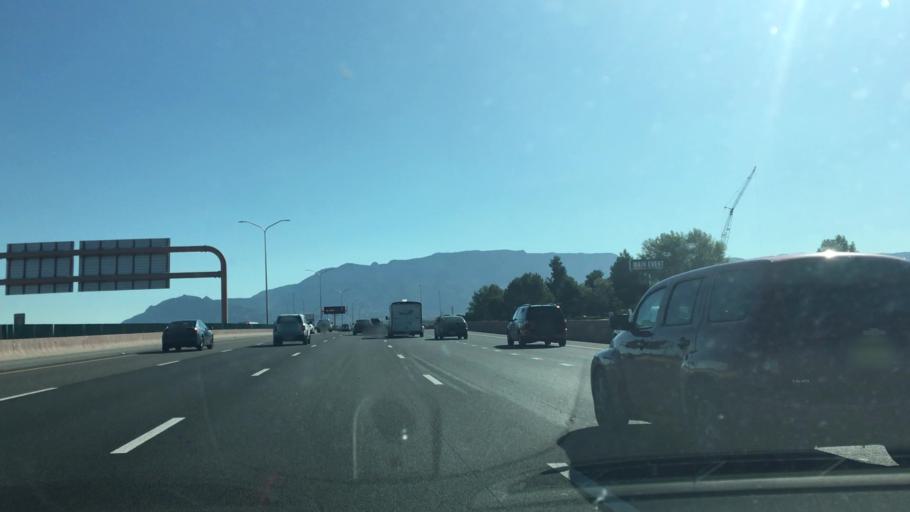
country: US
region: New Mexico
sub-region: Bernalillo County
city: Lee Acres
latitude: 35.1278
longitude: -106.6174
